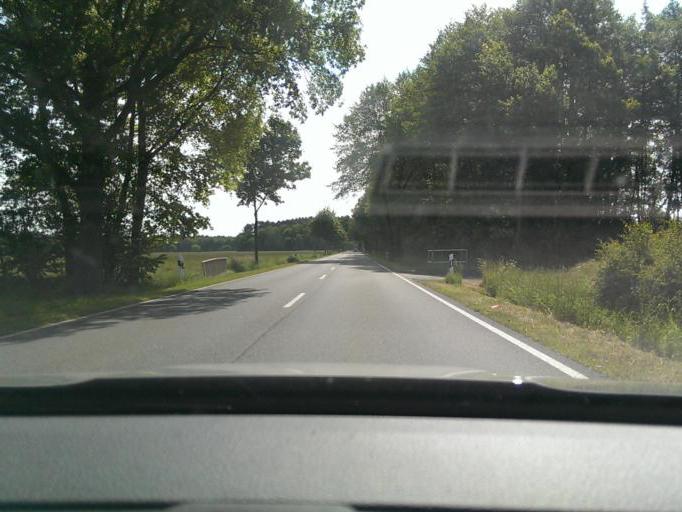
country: DE
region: Lower Saxony
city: Lindwedel
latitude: 52.6696
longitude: 9.7190
